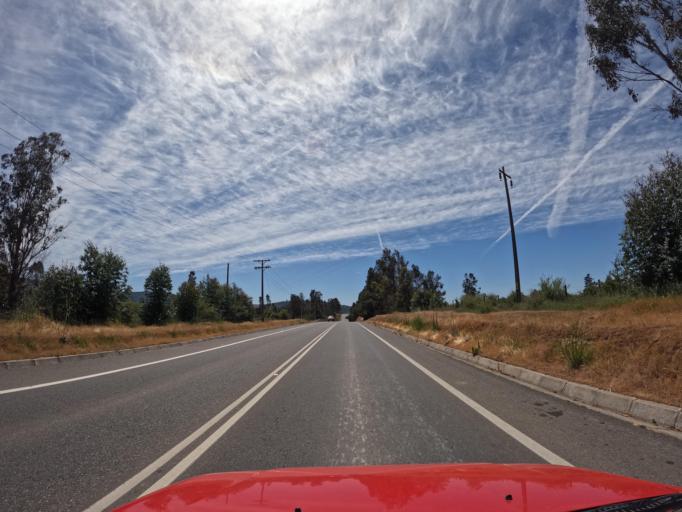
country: CL
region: Maule
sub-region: Provincia de Talca
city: Talca
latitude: -35.2880
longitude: -71.5310
